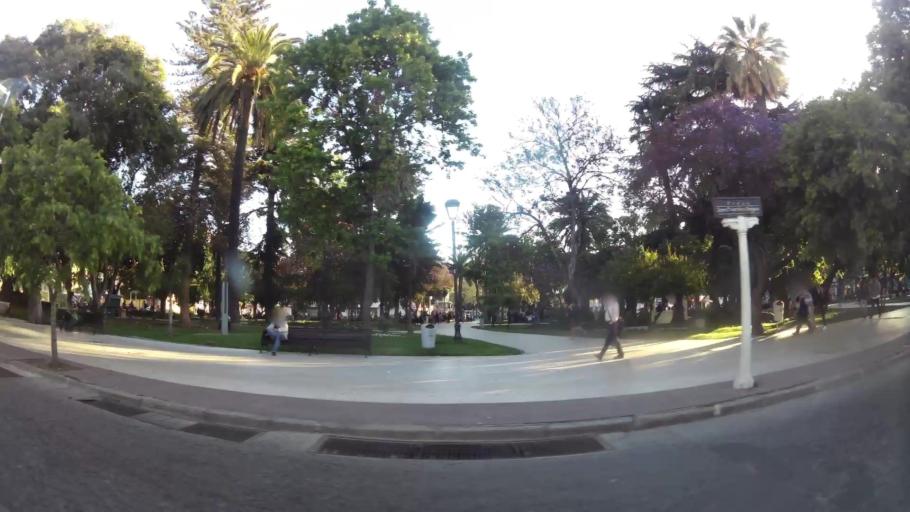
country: CL
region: Valparaiso
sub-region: Provincia de Valparaiso
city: Vina del Mar
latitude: -33.0240
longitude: -71.5517
